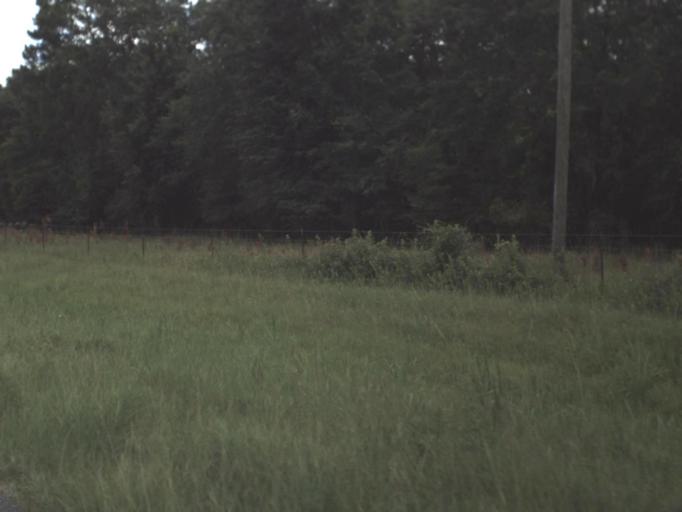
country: US
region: Florida
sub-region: Union County
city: Lake Butler
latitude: 29.9040
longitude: -82.3650
